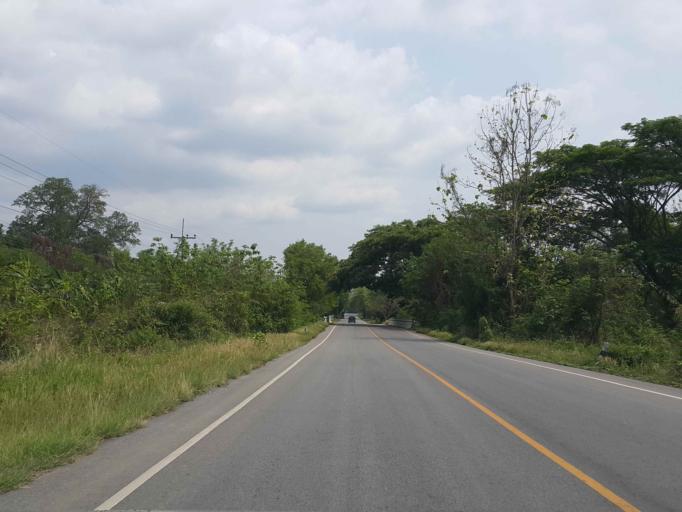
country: TH
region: Lampang
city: Thoen
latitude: 17.4906
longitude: 99.3491
